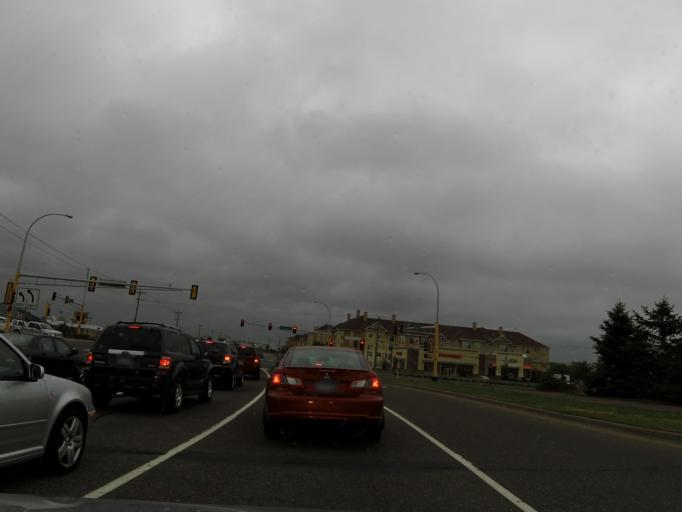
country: US
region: Minnesota
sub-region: Washington County
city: Lake Elmo
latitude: 44.9449
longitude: -92.9042
